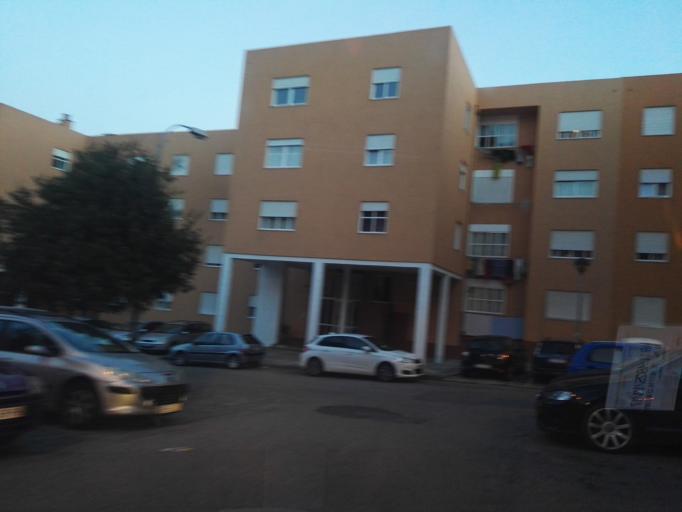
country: PT
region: Lisbon
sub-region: Lisbon
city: Lisbon
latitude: 38.7295
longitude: -9.1739
